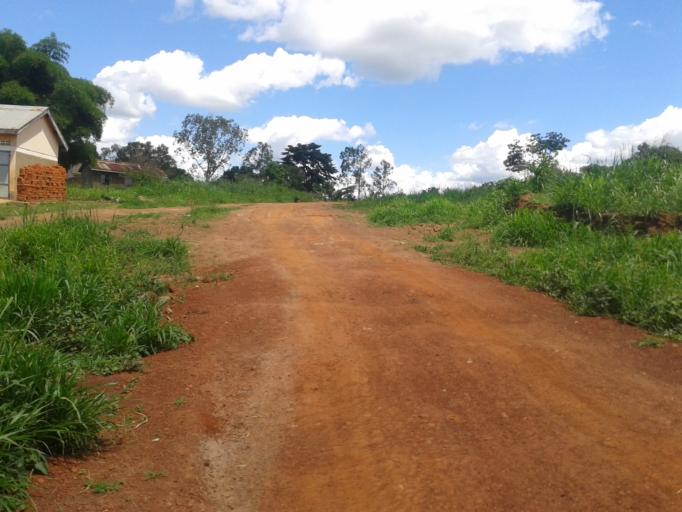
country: UG
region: Northern Region
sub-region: Gulu District
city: Gulu
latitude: 2.7667
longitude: 32.3199
